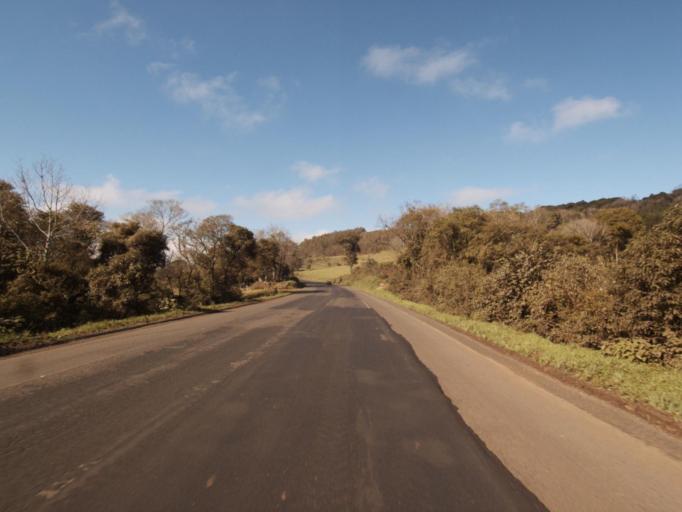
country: BR
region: Rio Grande do Sul
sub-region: Frederico Westphalen
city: Frederico Westphalen
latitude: -27.0542
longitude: -53.2286
